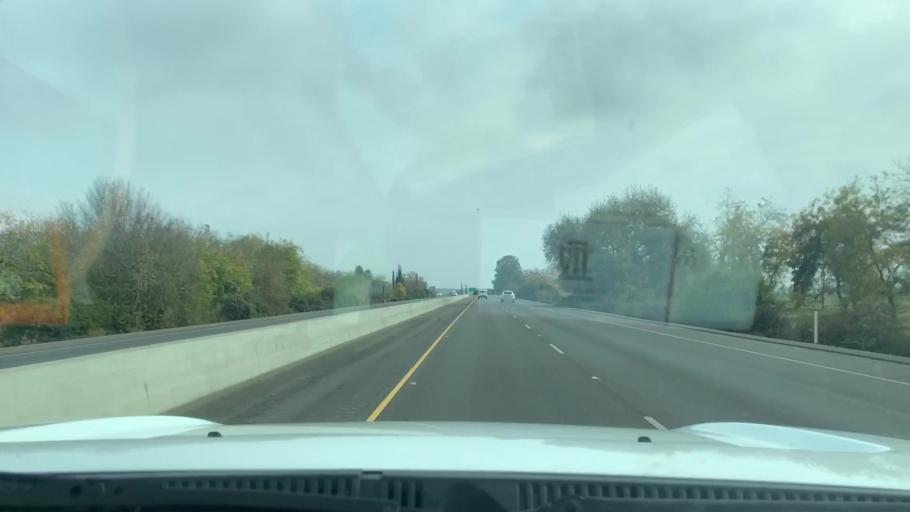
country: US
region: California
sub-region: Kings County
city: Lemoore
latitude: 36.2926
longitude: -119.7739
